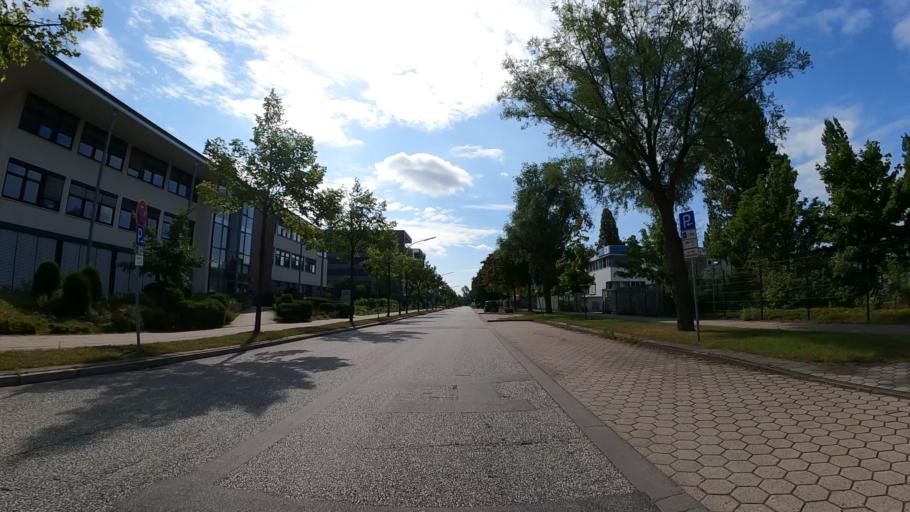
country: DE
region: Hamburg
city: Altona
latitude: 53.5390
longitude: 9.8630
